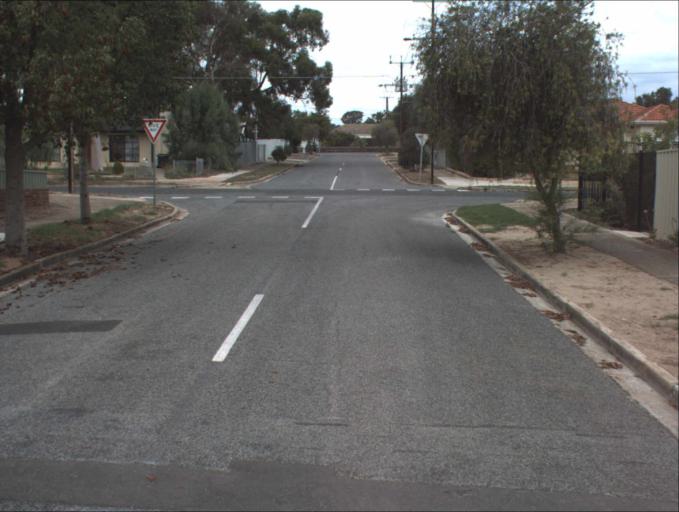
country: AU
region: South Australia
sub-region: Port Adelaide Enfield
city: Enfield
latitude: -34.8558
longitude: 138.6025
